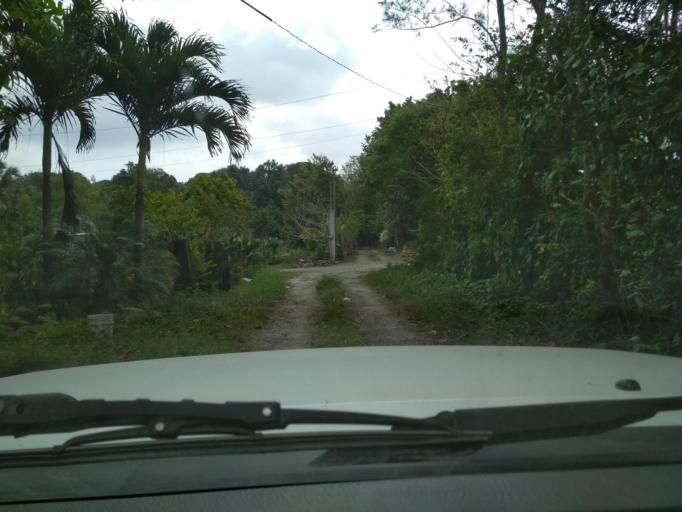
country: MX
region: Veracruz
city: El Tejar
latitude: 19.0803
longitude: -96.1701
